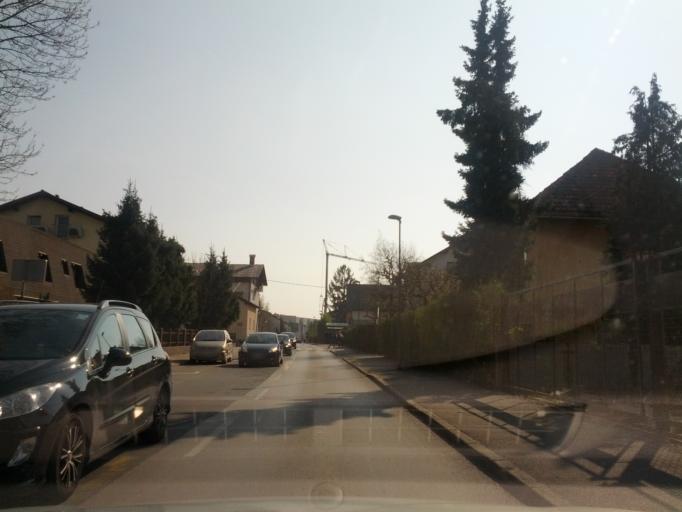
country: SI
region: Ljubljana
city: Ljubljana
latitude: 46.0717
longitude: 14.5370
